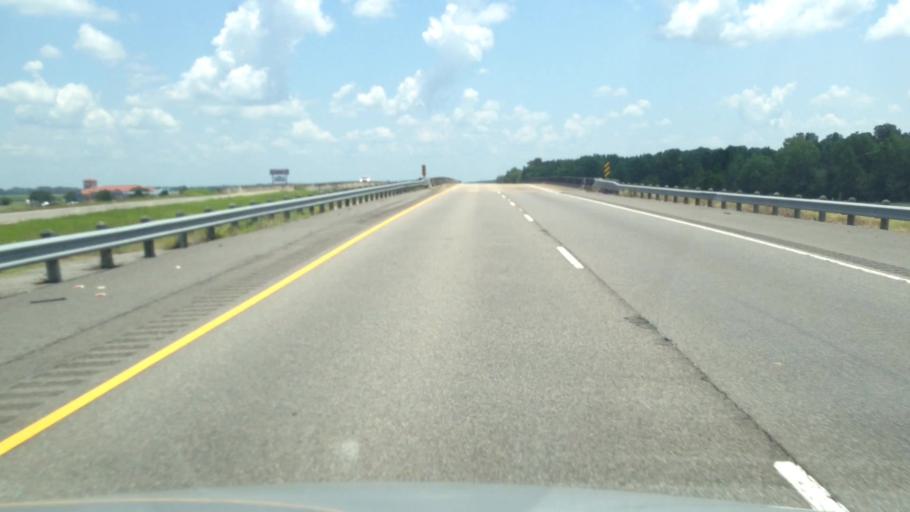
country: US
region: Louisiana
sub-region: Avoyelles Parish
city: Bunkie
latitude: 30.9528
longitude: -92.2769
